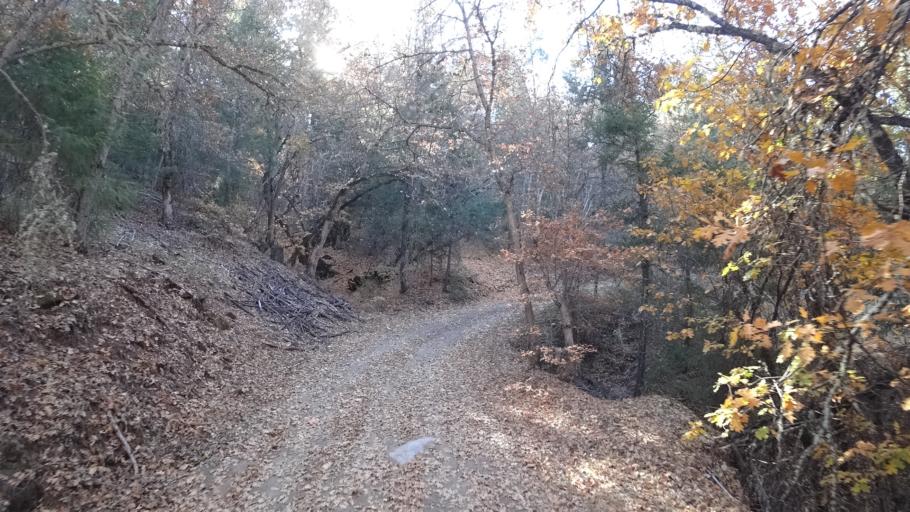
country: US
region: California
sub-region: Siskiyou County
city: Yreka
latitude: 41.8580
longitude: -122.7483
